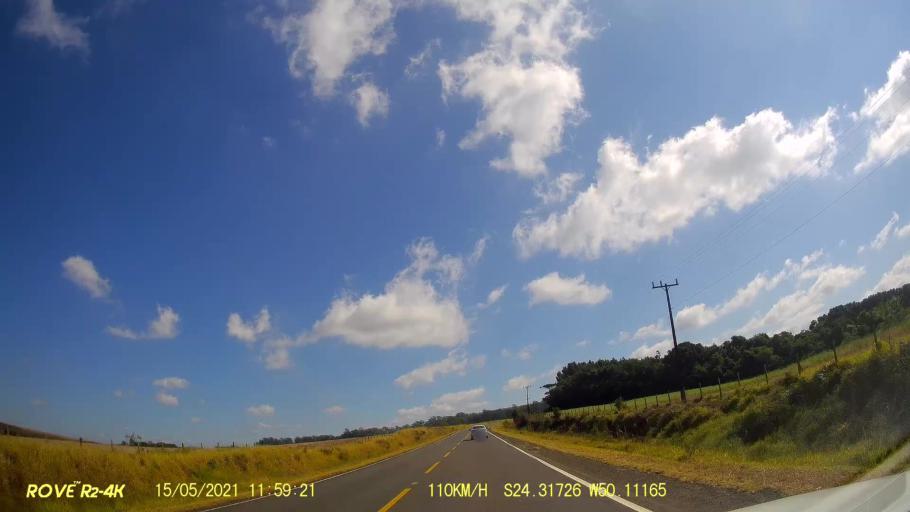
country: BR
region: Parana
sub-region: Pirai Do Sul
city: Pirai do Sul
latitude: -24.3173
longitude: -50.1116
